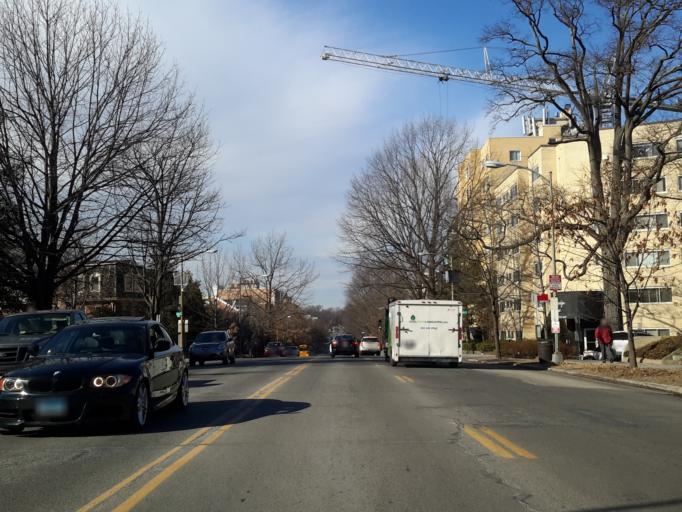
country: US
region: Maryland
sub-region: Montgomery County
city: Chevy Chase Village
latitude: 38.9592
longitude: -77.0722
